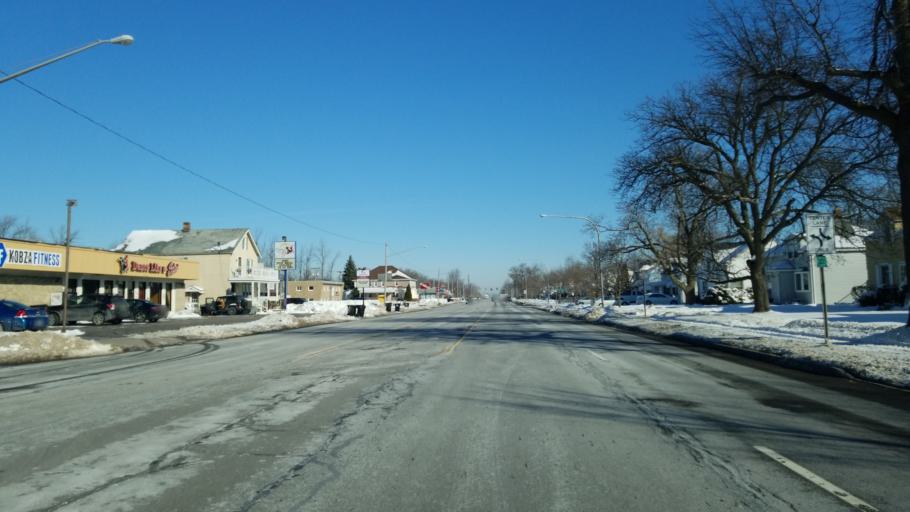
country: US
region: New York
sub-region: Erie County
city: Eggertsville
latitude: 42.9656
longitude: -78.8235
